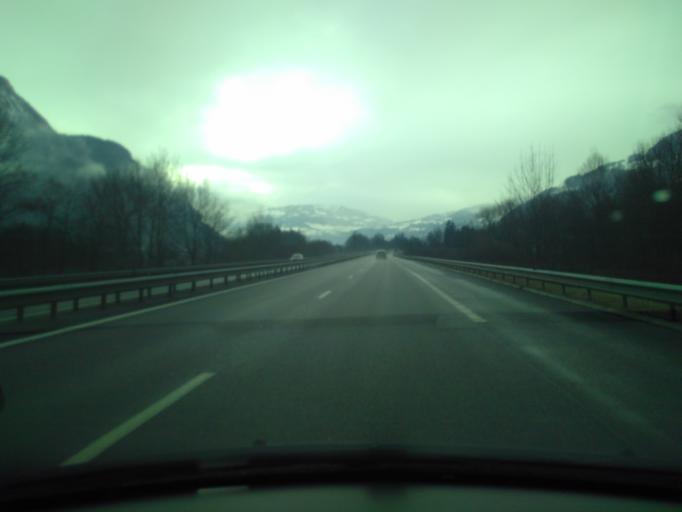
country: FR
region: Rhone-Alpes
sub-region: Departement de la Haute-Savoie
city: Sallanches
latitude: 45.9803
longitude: 6.6286
